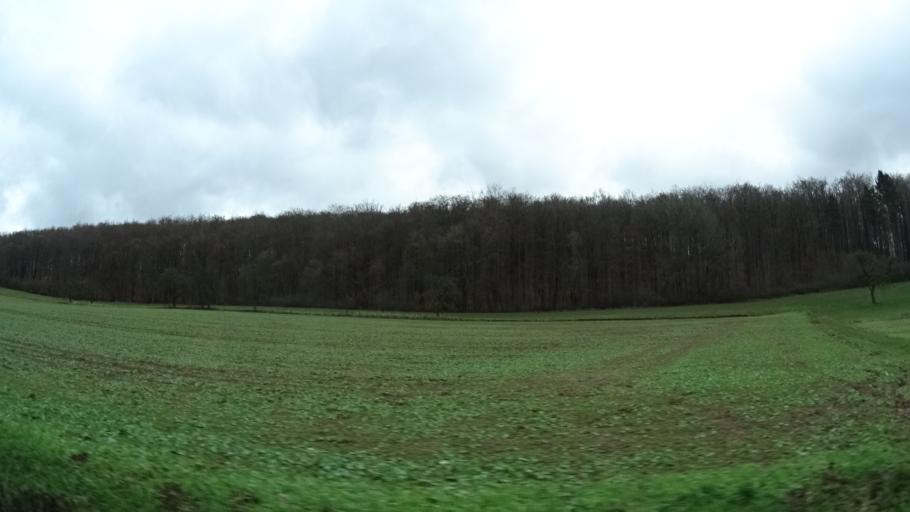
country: DE
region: Thuringia
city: Oberkatz
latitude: 50.5531
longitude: 10.2341
